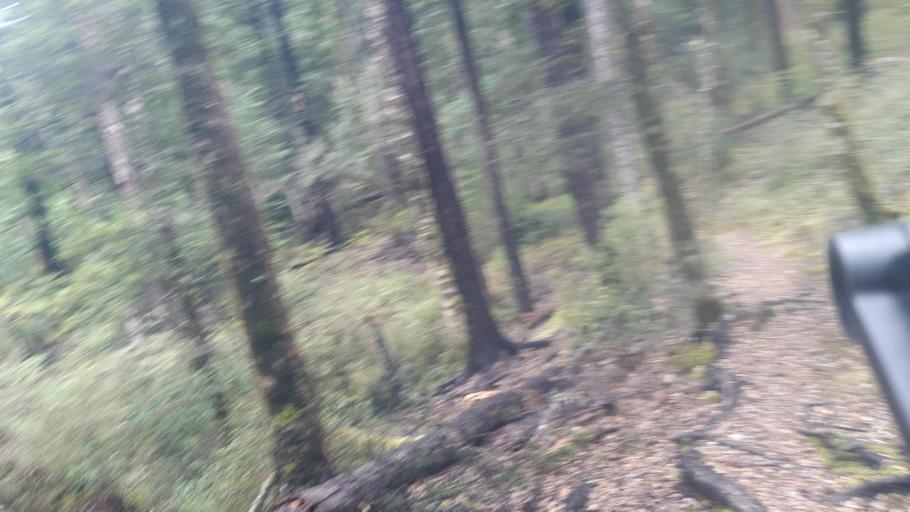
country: NZ
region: Tasman
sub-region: Tasman District
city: Wakefield
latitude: -41.7738
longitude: 172.8073
